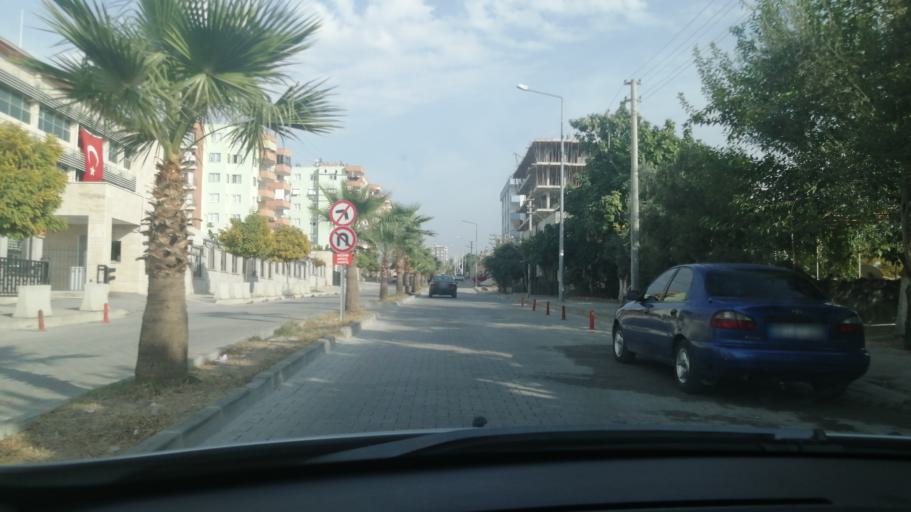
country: TR
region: Adana
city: Kadirli
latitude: 37.3724
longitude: 36.0770
